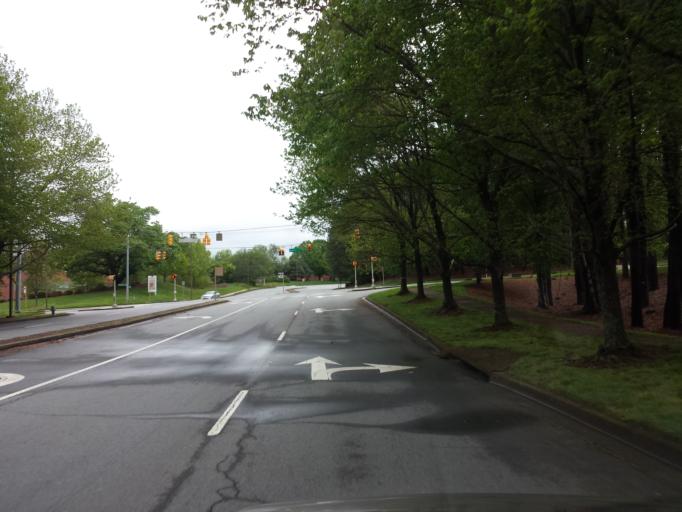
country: US
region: Georgia
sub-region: Cobb County
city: Kennesaw
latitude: 34.0037
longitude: -84.5865
